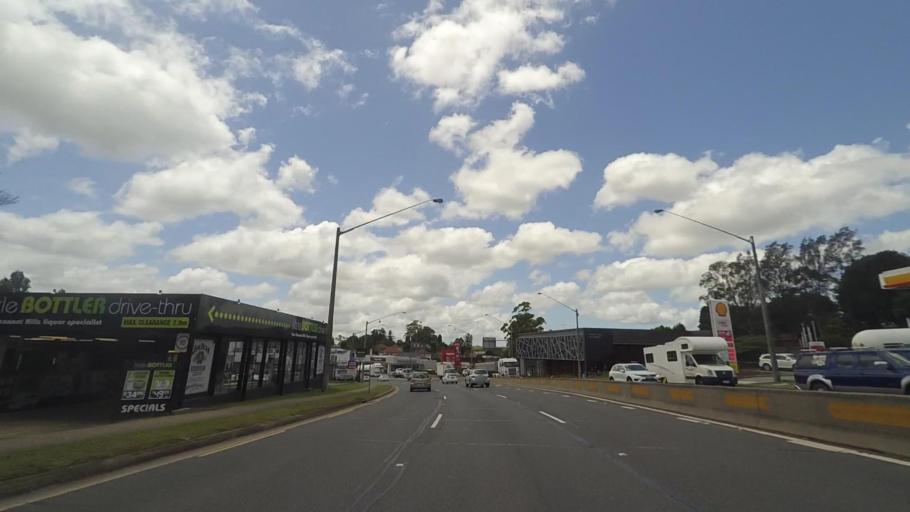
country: AU
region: New South Wales
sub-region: Hornsby Shire
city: Pennant Hills
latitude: -33.7386
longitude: 151.0732
